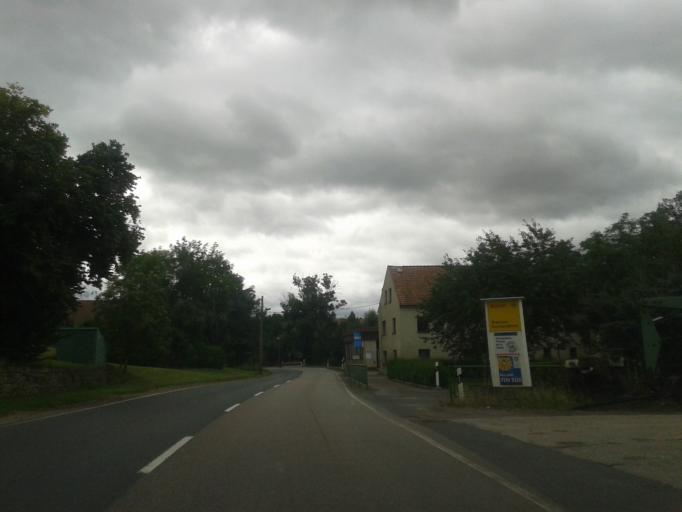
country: DE
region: Saxony
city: Wilsdruff
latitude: 51.0212
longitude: 13.5577
